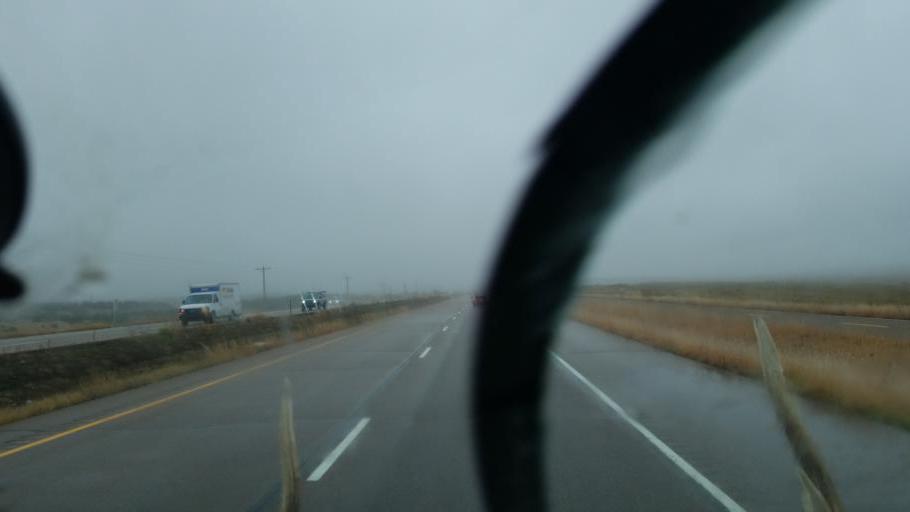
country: US
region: Colorado
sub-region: Pueblo County
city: Pueblo
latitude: 38.1027
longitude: -104.6837
